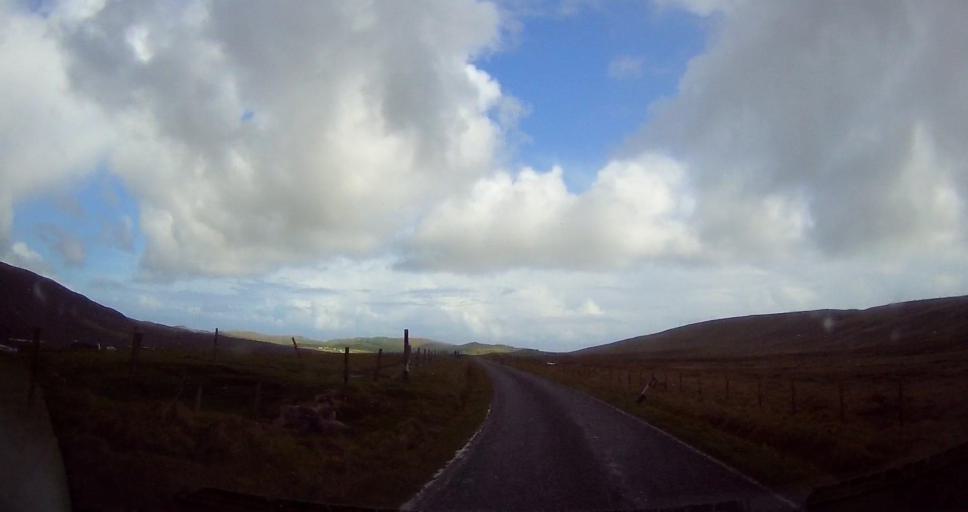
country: GB
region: Scotland
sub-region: Shetland Islands
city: Lerwick
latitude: 60.5596
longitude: -1.3368
